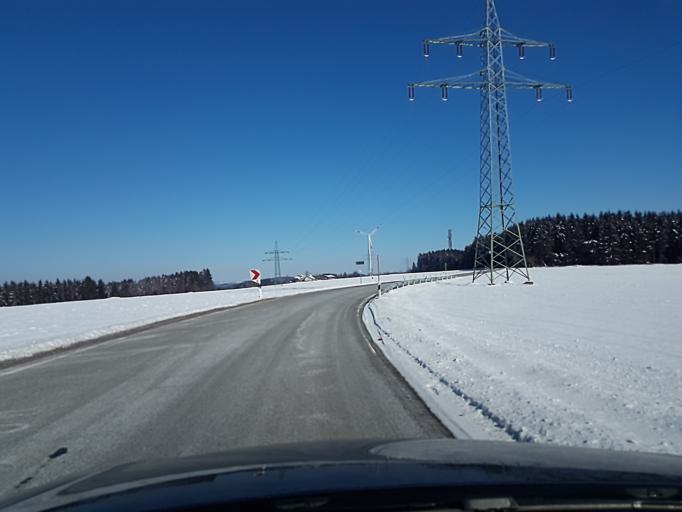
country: DE
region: Baden-Wuerttemberg
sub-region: Freiburg Region
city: Tennenbronn
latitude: 48.1647
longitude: 8.3549
